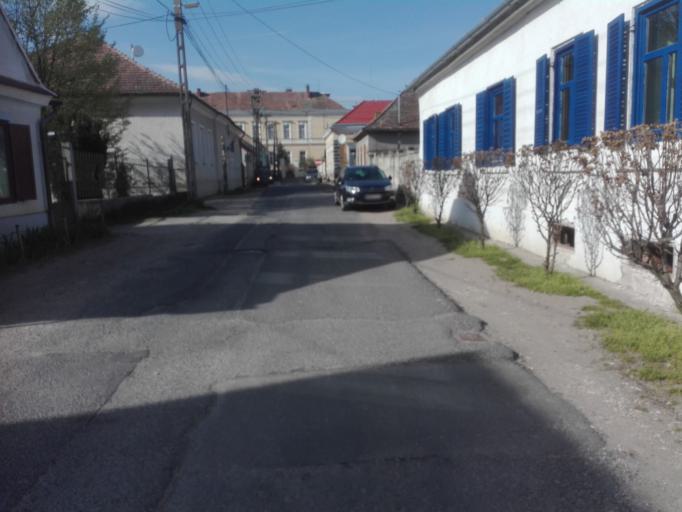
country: HU
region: Vas
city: Kormend
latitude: 47.0079
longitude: 16.6021
